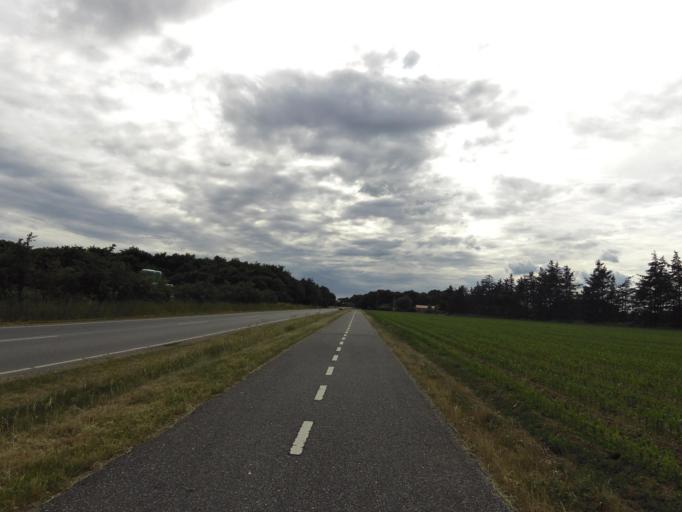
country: DK
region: South Denmark
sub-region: Esbjerg Kommune
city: Ribe
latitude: 55.3345
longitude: 8.8057
